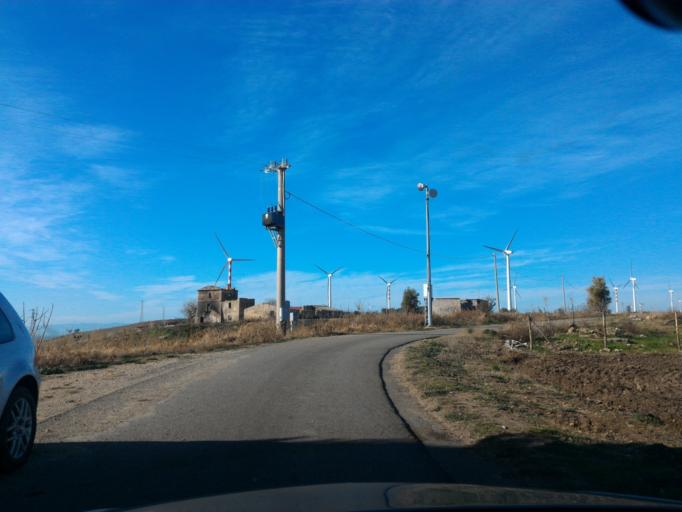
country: IT
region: Calabria
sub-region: Provincia di Crotone
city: Isola di Capo Rizzuto
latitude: 38.9452
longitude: 17.0578
